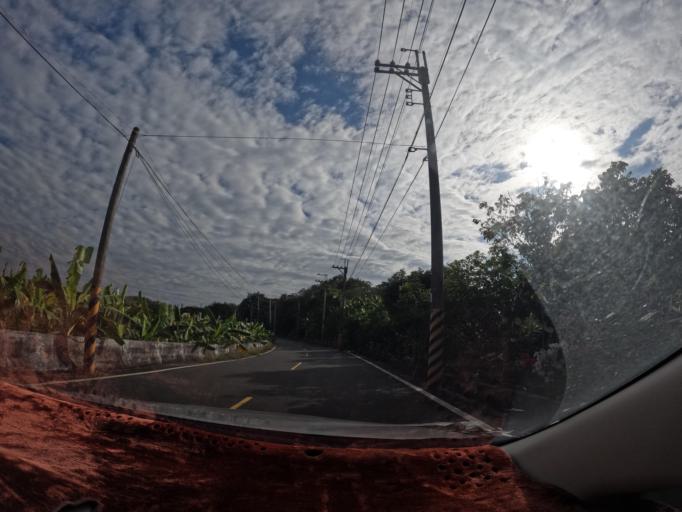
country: TW
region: Taiwan
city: Yujing
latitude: 23.0307
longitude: 120.4146
